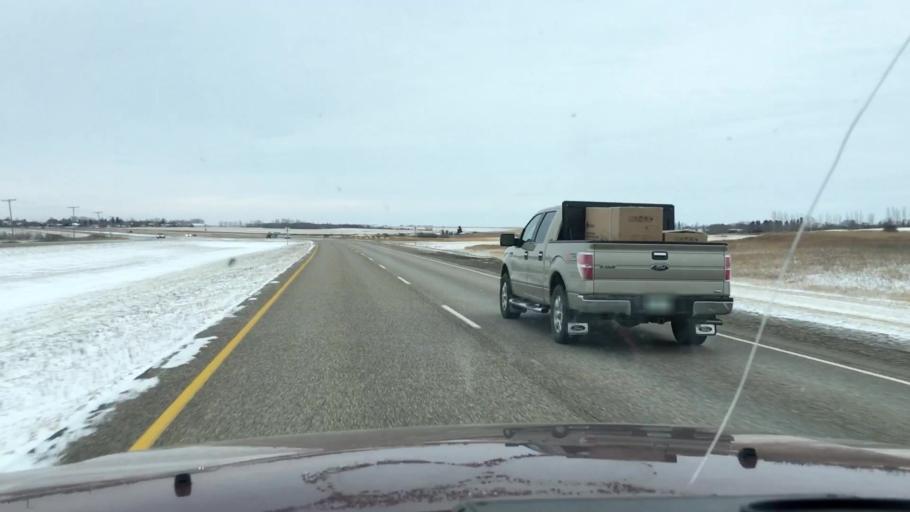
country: CA
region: Saskatchewan
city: Moose Jaw
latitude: 50.9516
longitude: -105.7079
